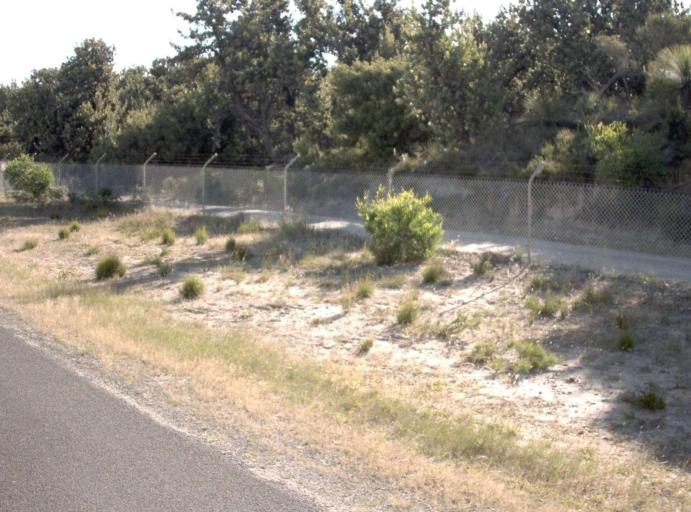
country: AU
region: Victoria
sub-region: Latrobe
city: Morwell
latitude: -38.7124
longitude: 146.3963
